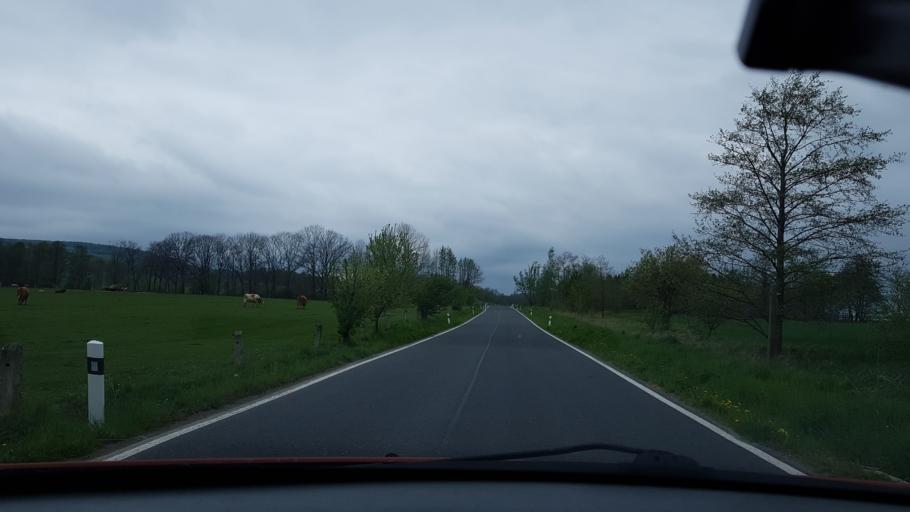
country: PL
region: Opole Voivodeship
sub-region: Powiat nyski
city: Kamienica
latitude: 50.4271
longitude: 16.9604
